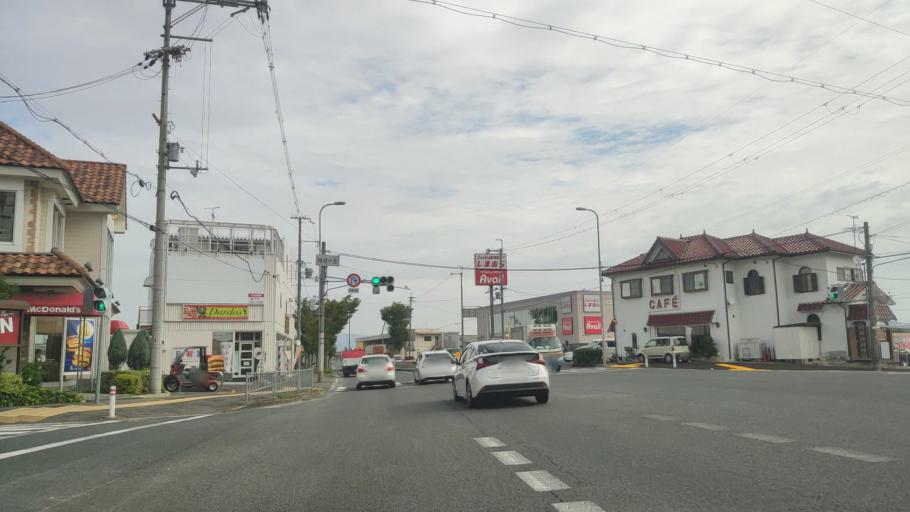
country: JP
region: Osaka
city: Tondabayashicho
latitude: 34.5136
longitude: 135.6042
